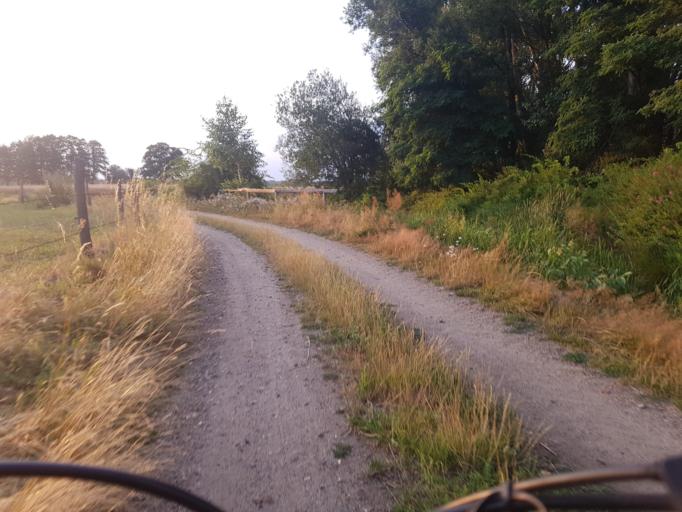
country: DE
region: Brandenburg
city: Bad Liebenwerda
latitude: 51.5598
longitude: 13.4054
